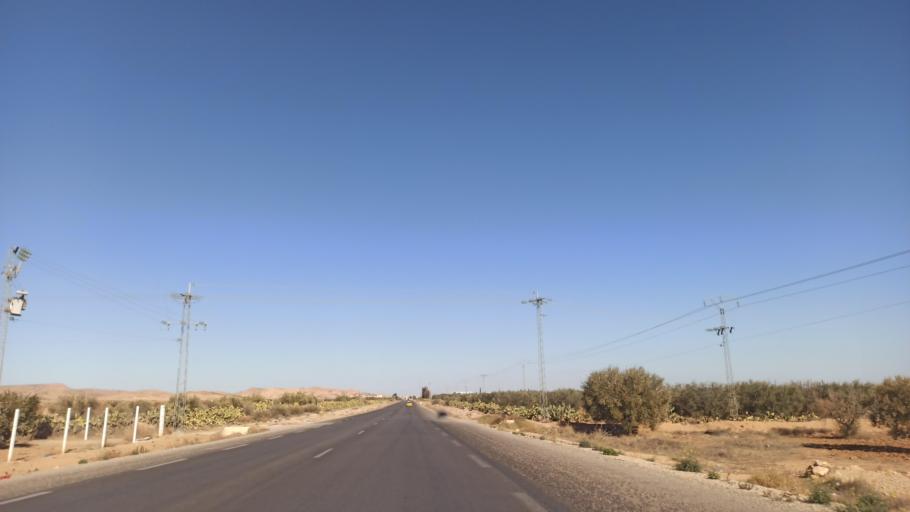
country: TN
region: Sidi Bu Zayd
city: Bi'r al Hufayy
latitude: 34.8944
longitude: 9.1710
